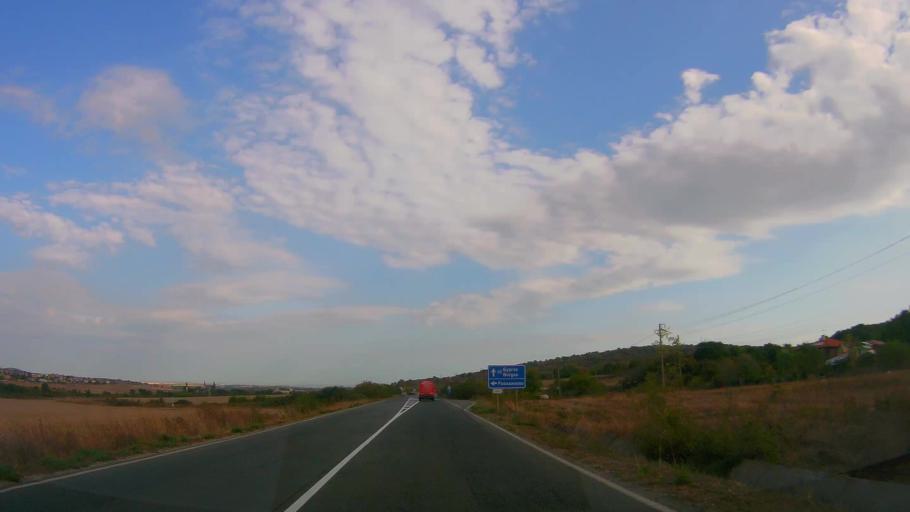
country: BG
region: Burgas
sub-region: Obshtina Sozopol
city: Sozopol
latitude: 42.3773
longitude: 27.6820
